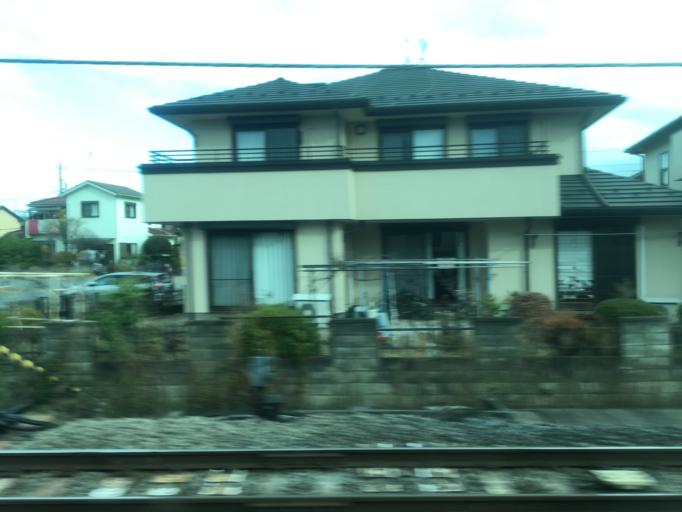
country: JP
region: Saitama
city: Fukiage-fujimi
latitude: 36.1017
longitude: 139.4569
